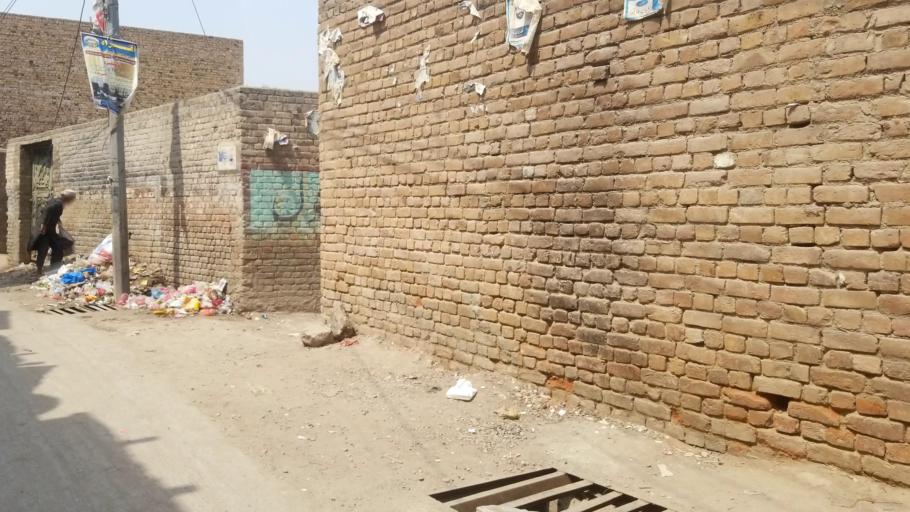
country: PK
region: Khyber Pakhtunkhwa
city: Peshawar
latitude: 33.9909
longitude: 71.5438
